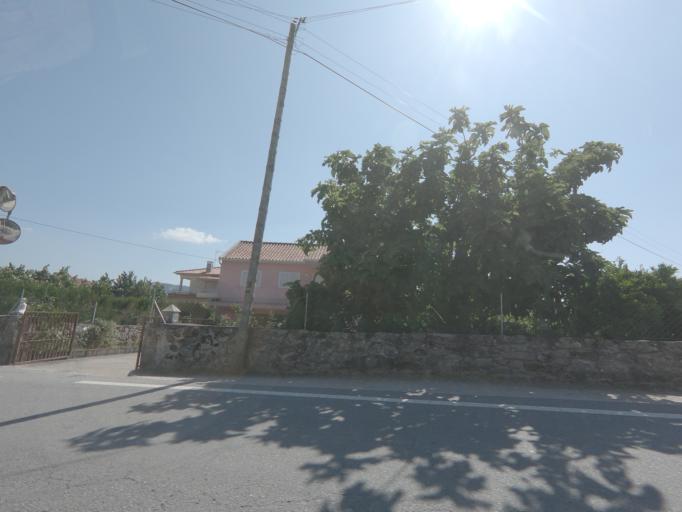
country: PT
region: Viseu
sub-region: Tarouca
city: Tarouca
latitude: 41.0307
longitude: -7.7474
